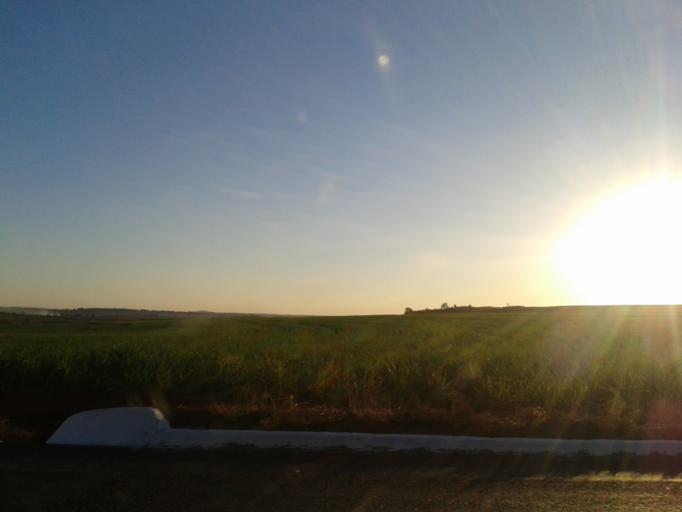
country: BR
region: Minas Gerais
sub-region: Centralina
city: Centralina
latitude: -18.7220
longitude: -49.2791
